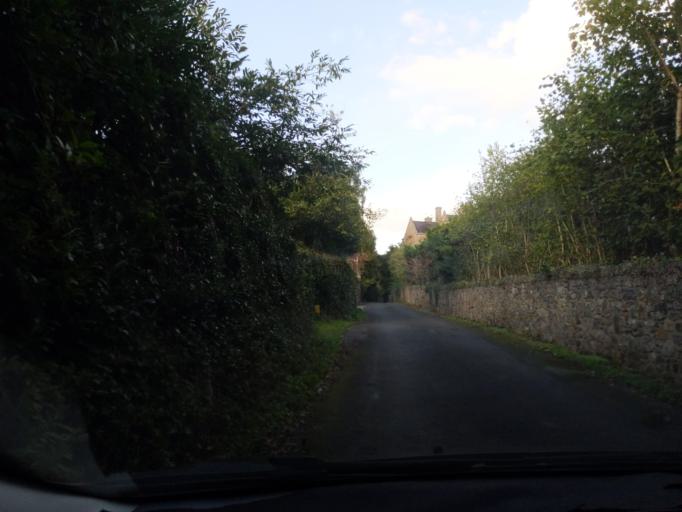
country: GB
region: England
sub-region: Devon
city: Bovey Tracey
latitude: 50.6357
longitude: -3.6455
